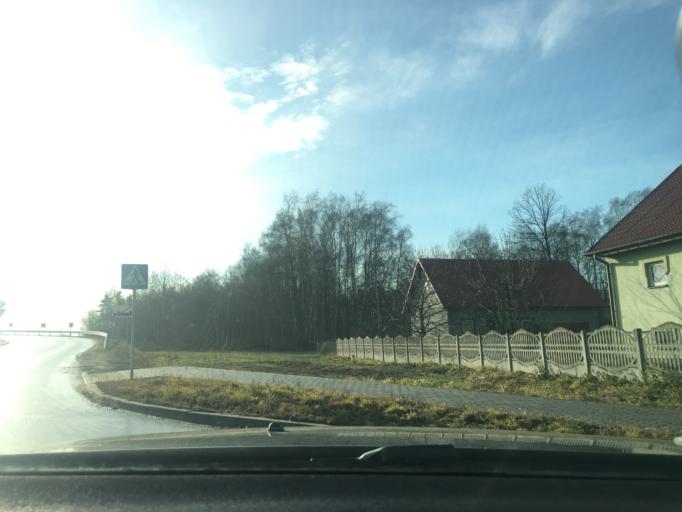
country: PL
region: Swietokrzyskie
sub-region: Powiat jedrzejowski
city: Jedrzejow
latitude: 50.6622
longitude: 20.3283
